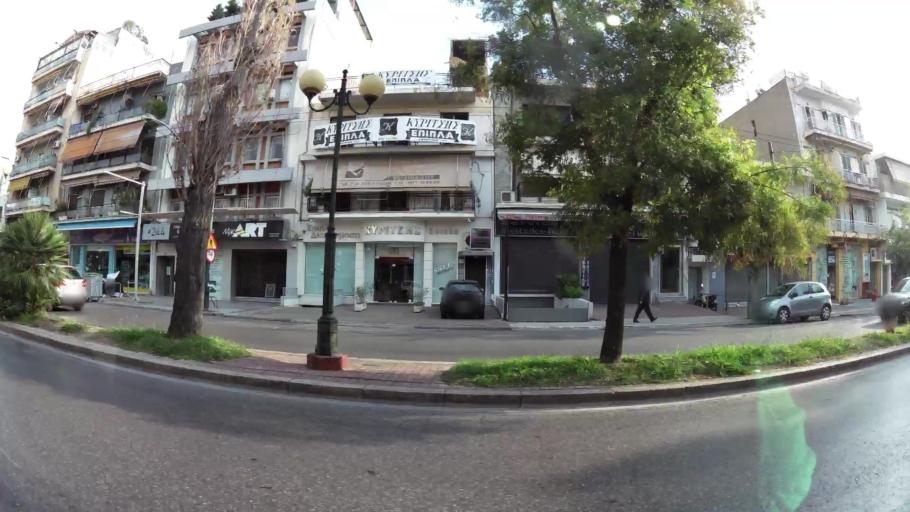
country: GR
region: Attica
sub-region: Nomarchia Athinas
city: Athens
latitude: 37.9994
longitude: 23.7079
